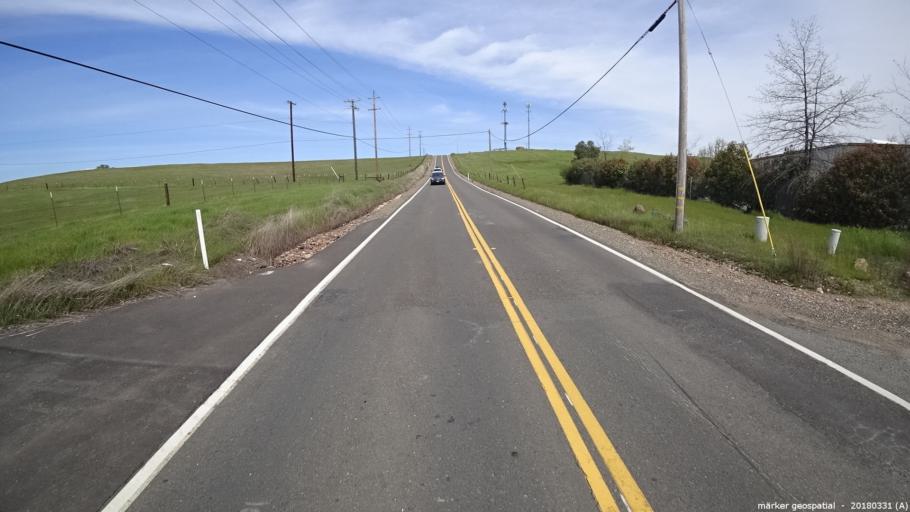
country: US
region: California
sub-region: Sacramento County
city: Rancho Murieta
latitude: 38.5106
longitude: -121.1020
